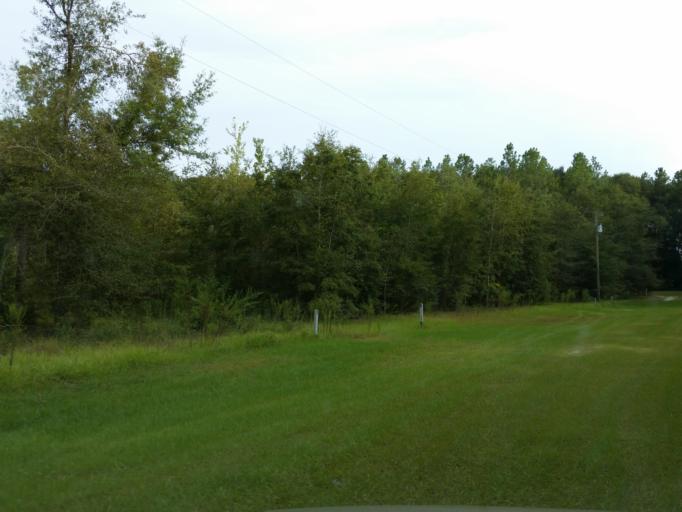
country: US
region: Florida
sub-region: Madison County
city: Madison
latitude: 30.5319
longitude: -83.2130
